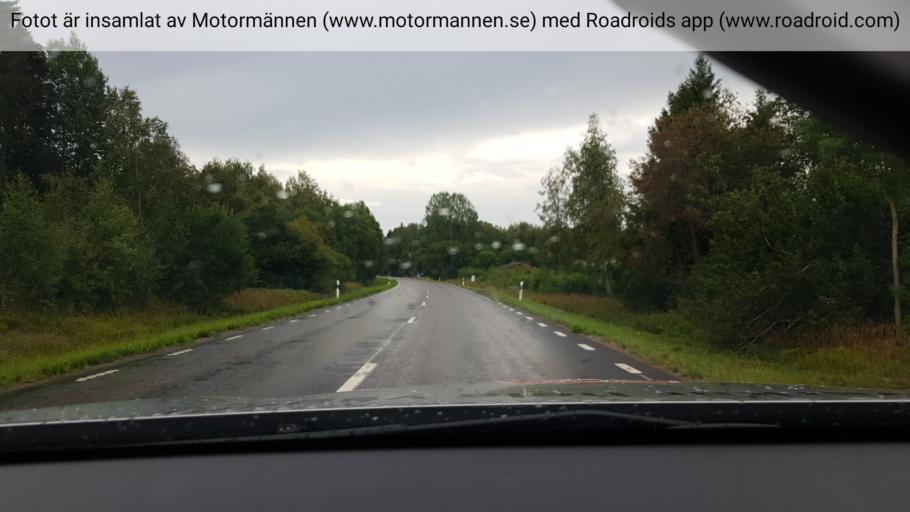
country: SE
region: Uppsala
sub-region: Tierps Kommun
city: Karlholmsbruk
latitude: 60.5220
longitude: 17.6059
